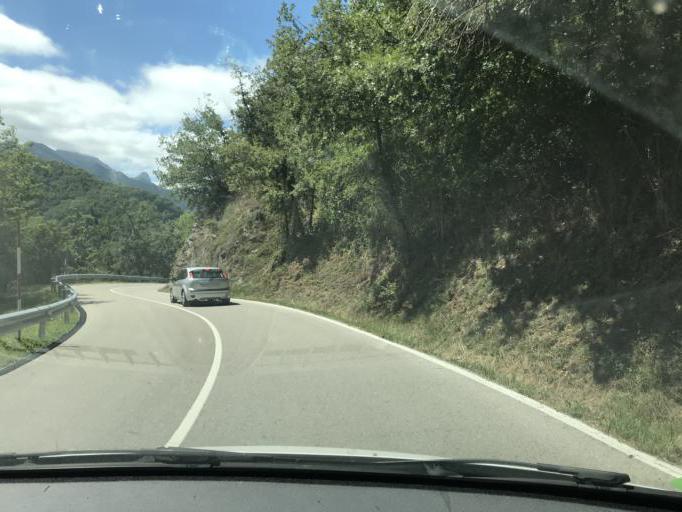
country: ES
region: Cantabria
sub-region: Provincia de Cantabria
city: Cabezon de Liebana
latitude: 43.0756
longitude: -4.5013
